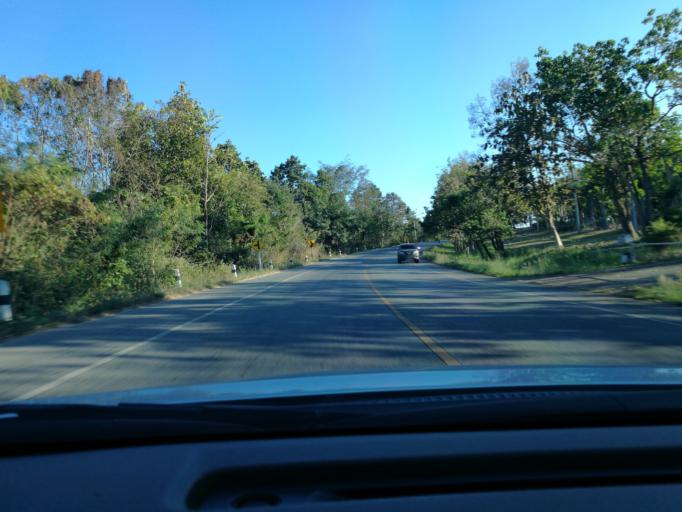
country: TH
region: Phitsanulok
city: Nakhon Thai
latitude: 17.0348
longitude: 100.8186
